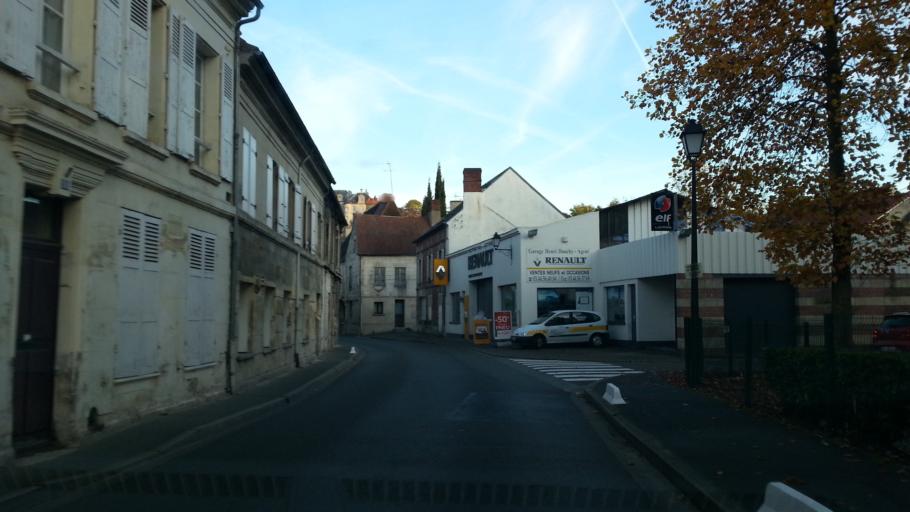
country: FR
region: Picardie
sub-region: Departement de l'Oise
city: Cires-les-Mello
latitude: 49.2725
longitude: 2.3628
